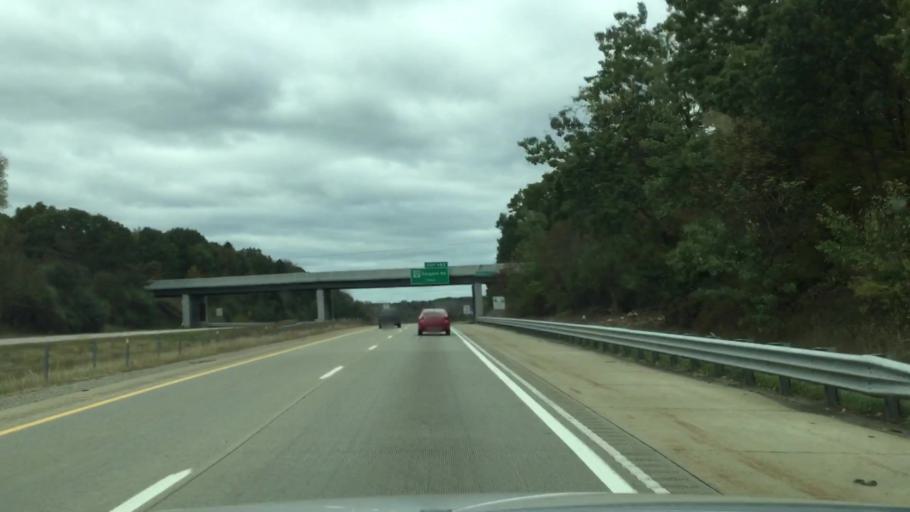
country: US
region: Michigan
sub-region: Jackson County
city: Michigan Center
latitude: 42.2849
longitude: -84.2835
